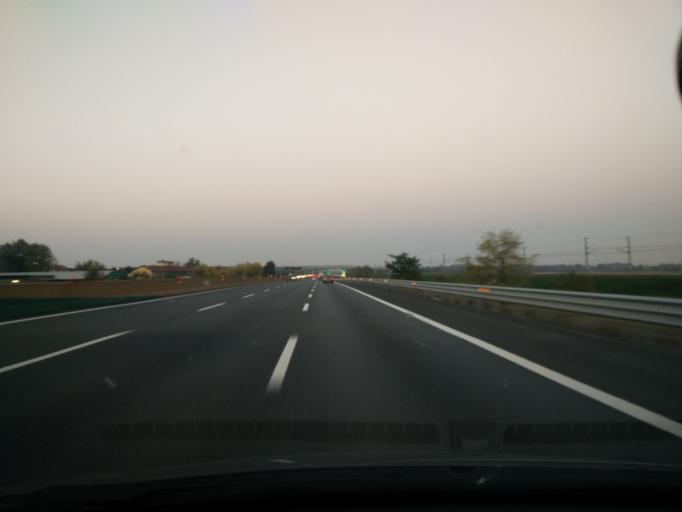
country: IT
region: Piedmont
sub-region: Provincia di Vercelli
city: Santhia
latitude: 45.4006
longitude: 8.1590
